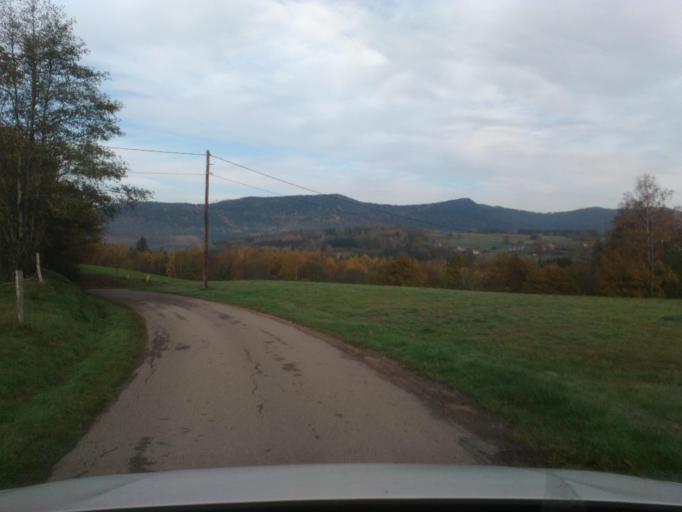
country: FR
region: Lorraine
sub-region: Departement des Vosges
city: Moyenmoutier
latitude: 48.3612
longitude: 6.9272
